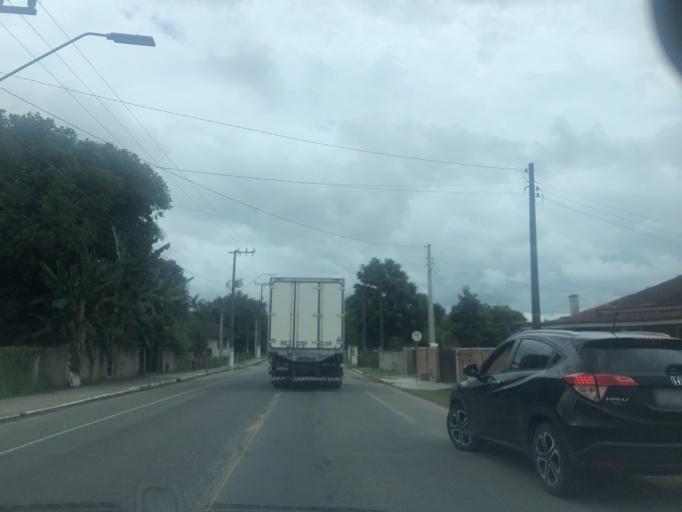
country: BR
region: Santa Catarina
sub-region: Joinville
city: Joinville
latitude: -26.3801
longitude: -48.7256
